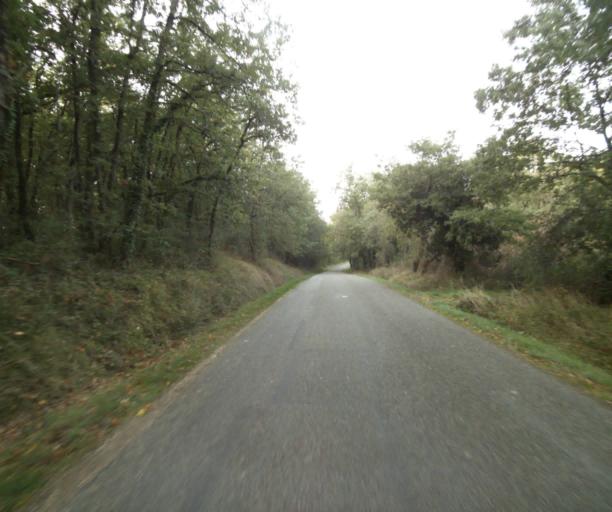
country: FR
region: Midi-Pyrenees
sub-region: Departement du Tarn-et-Garonne
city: Campsas
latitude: 43.8712
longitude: 1.3420
